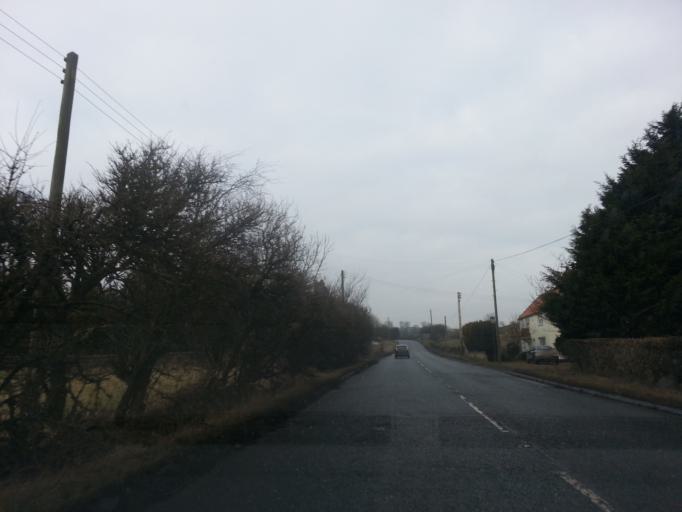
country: GB
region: England
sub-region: Darlington
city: Walworth
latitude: 54.5856
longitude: -1.6333
